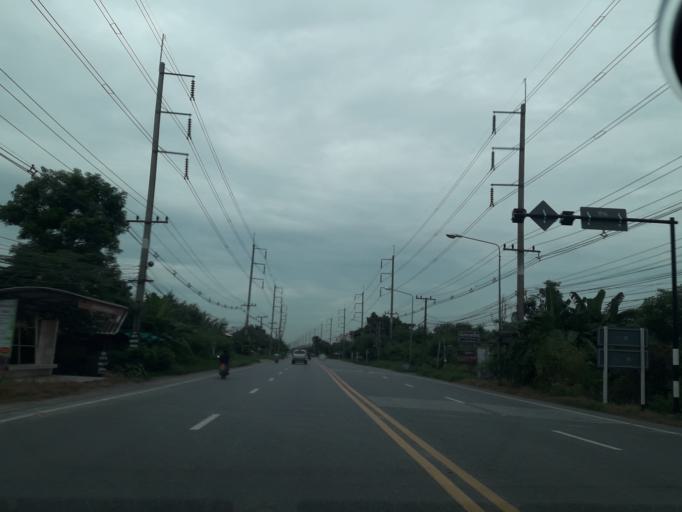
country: TH
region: Pathum Thani
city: Ban Lam Luk Ka
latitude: 13.9507
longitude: 100.8133
